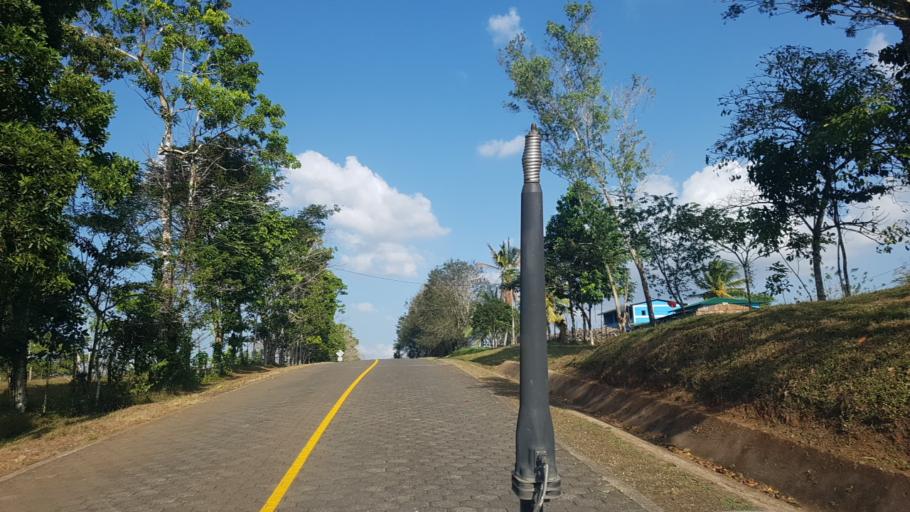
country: NI
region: Atlantico Sur
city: Nueva Guinea
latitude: 11.6910
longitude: -84.4196
